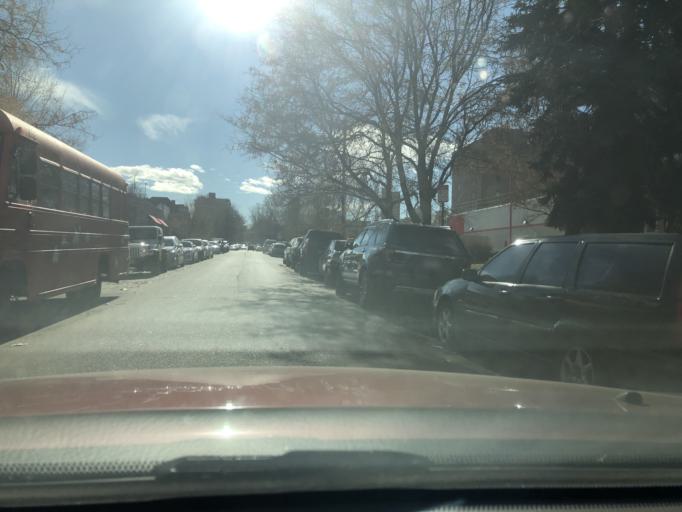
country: US
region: Colorado
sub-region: Denver County
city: Denver
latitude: 39.7411
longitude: -104.9610
